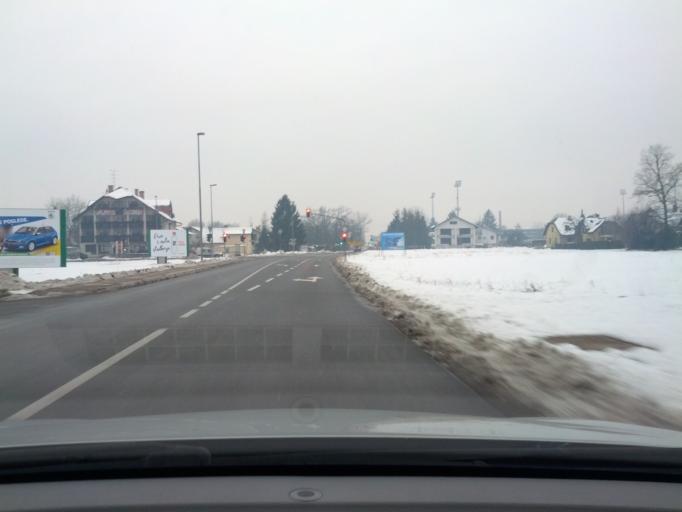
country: SI
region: Domzale
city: Domzale
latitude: 46.1354
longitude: 14.6075
